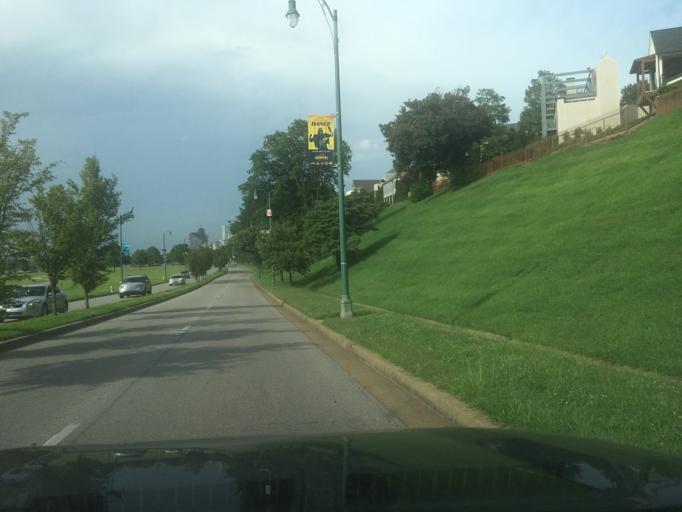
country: US
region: Tennessee
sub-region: Shelby County
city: Memphis
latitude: 35.1323
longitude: -90.0661
